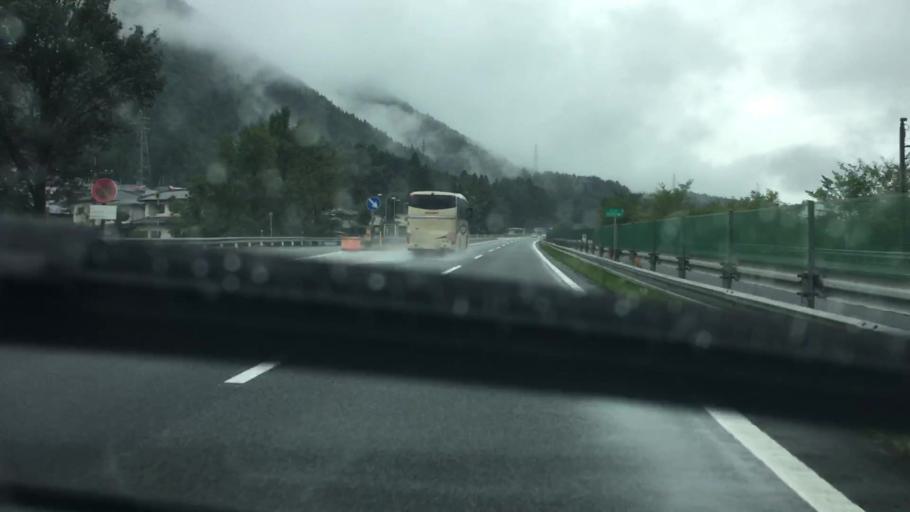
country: JP
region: Yamanashi
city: Otsuki
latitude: 35.5240
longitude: 138.8528
